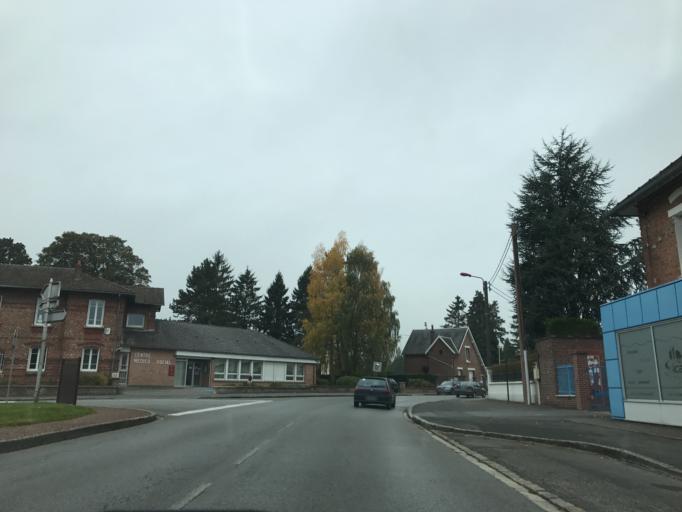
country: FR
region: Picardie
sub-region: Departement de la Somme
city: Peronne
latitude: 49.9355
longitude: 2.9311
